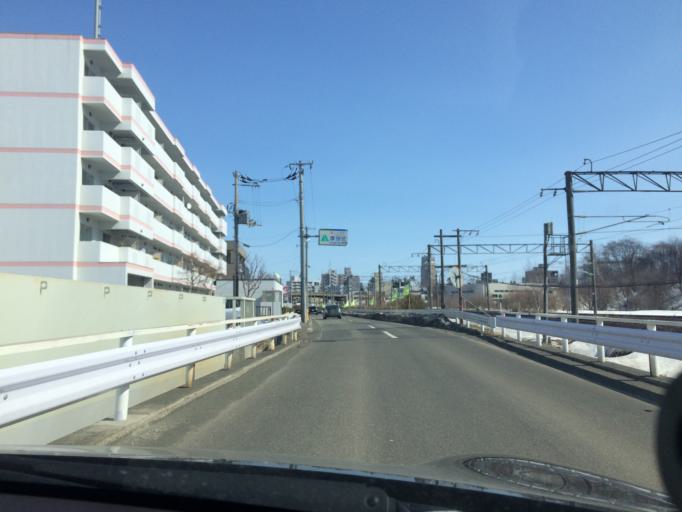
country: JP
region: Hokkaido
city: Sapporo
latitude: 43.0437
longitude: 141.4551
